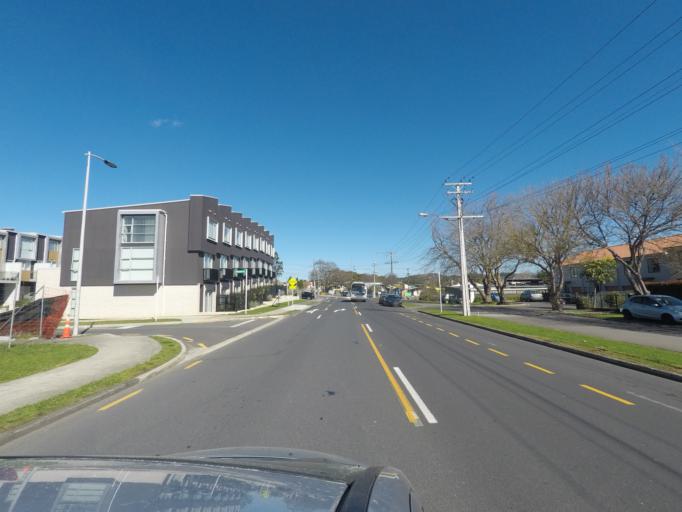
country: NZ
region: Auckland
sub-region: Auckland
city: Waitakere
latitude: -36.9127
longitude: 174.6819
